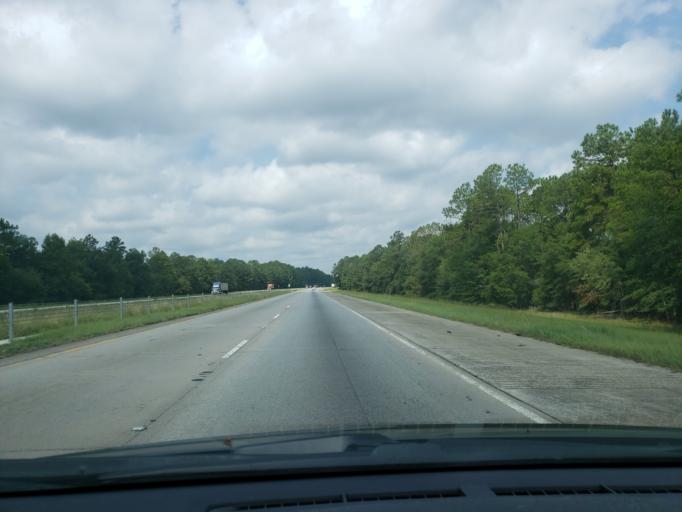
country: US
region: Georgia
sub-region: Emanuel County
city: Swainsboro
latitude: 32.4082
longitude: -82.3419
